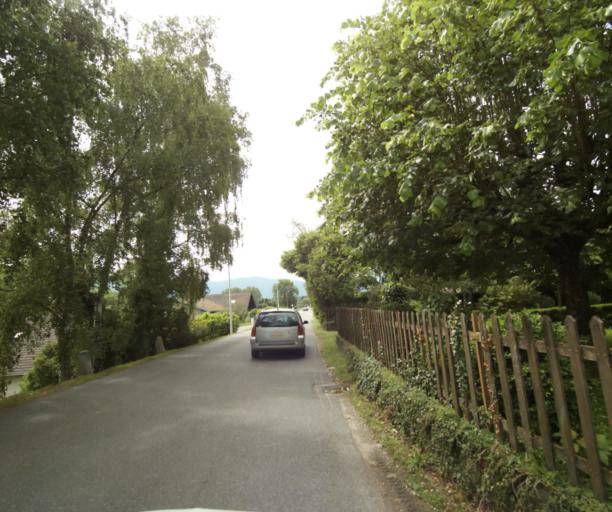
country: FR
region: Rhone-Alpes
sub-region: Departement de la Haute-Savoie
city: Margencel
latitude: 46.3377
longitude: 6.4331
